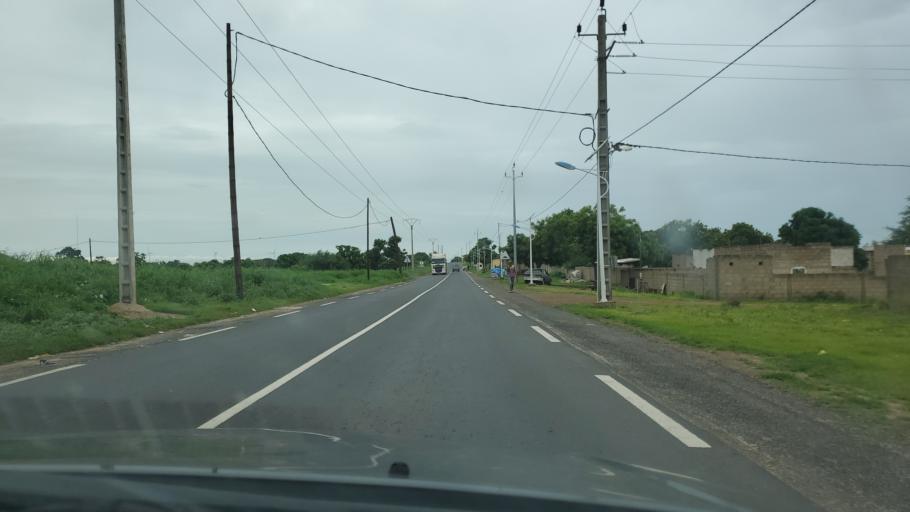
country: SN
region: Thies
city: Kayar
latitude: 15.0637
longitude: -16.9363
